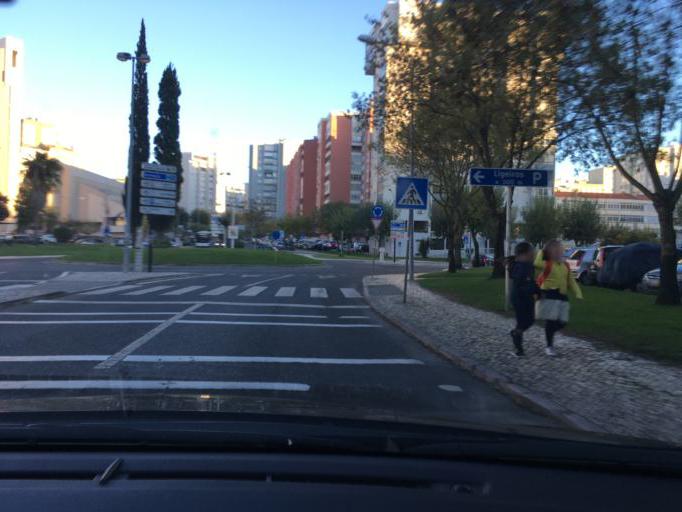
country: PT
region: Lisbon
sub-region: Odivelas
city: Pontinha
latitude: 38.7639
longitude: -9.2078
